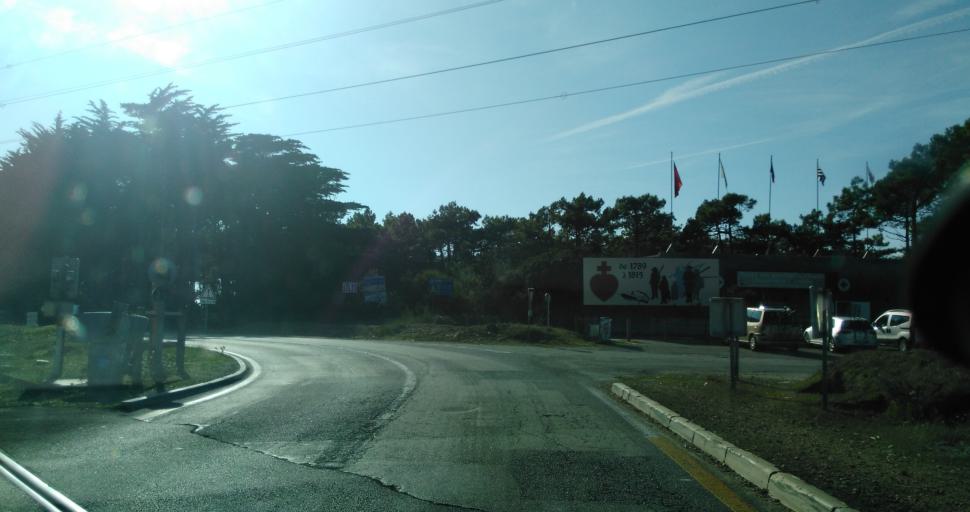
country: FR
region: Brittany
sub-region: Departement du Morbihan
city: Plouharnel
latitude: 47.5946
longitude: -3.1318
